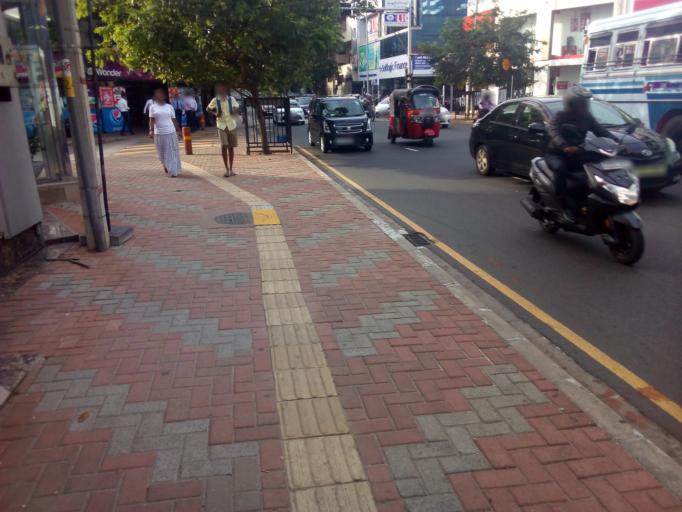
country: LK
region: Western
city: Pita Kotte
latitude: 6.8896
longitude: 79.8592
